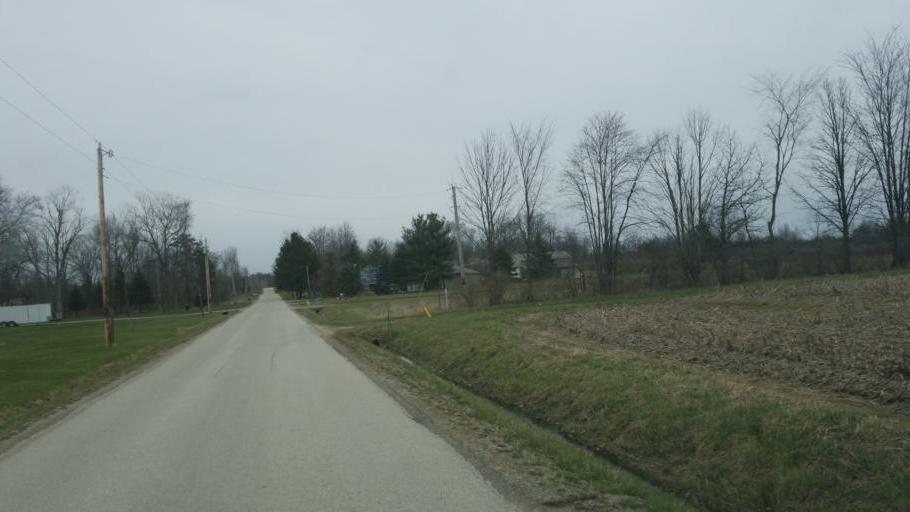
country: US
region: Ohio
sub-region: Knox County
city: Centerburg
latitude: 40.3281
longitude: -82.6478
